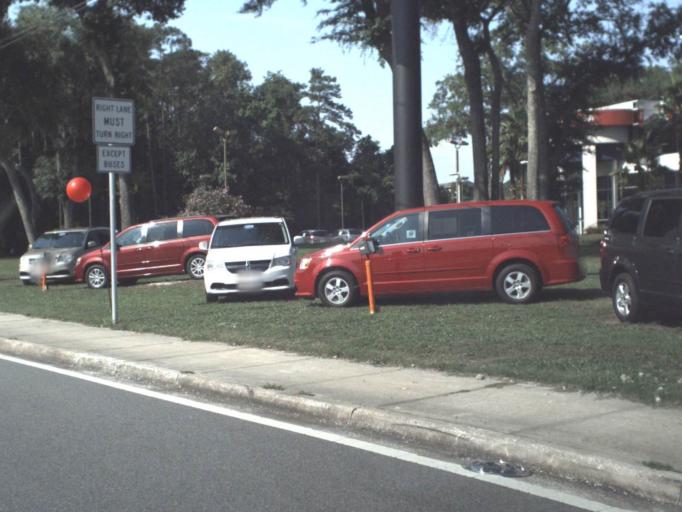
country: US
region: Florida
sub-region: Clay County
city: Bellair-Meadowbrook Terrace
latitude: 30.2337
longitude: -81.7394
